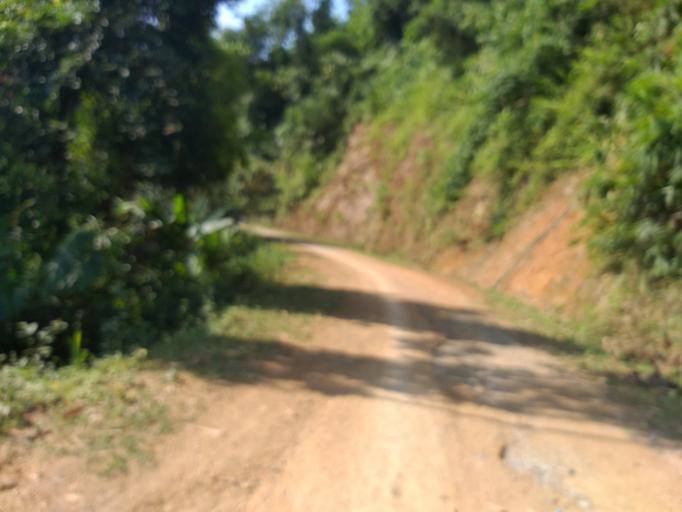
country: LA
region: Phongsali
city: Khoa
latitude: 21.1976
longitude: 102.6645
